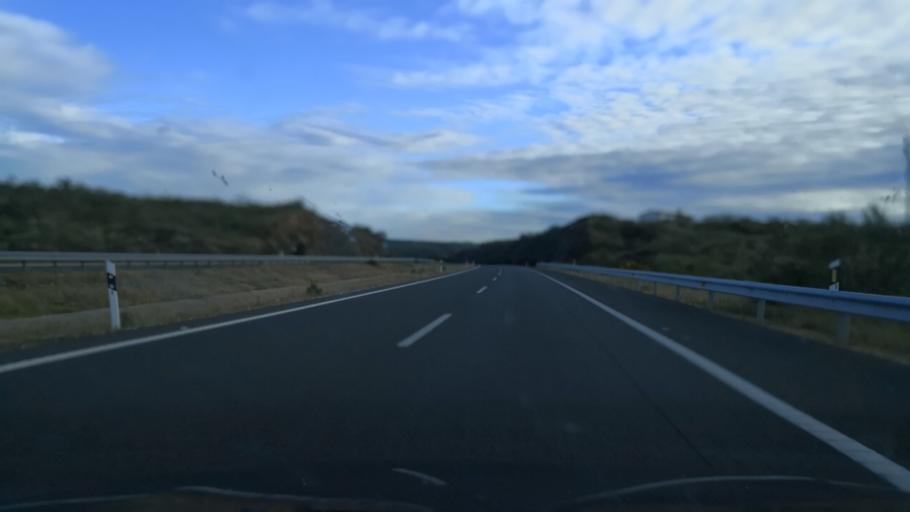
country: ES
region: Extremadura
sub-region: Provincia de Caceres
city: Hinojal
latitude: 39.7339
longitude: -6.4115
